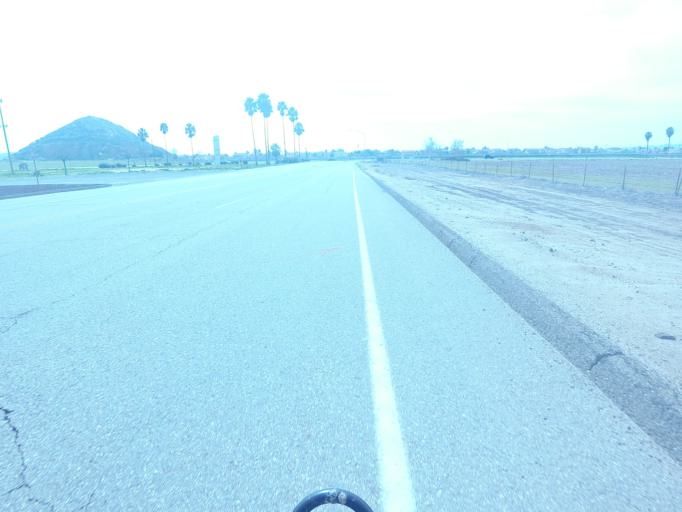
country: US
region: California
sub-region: Riverside County
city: Perris
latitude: 33.8464
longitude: -117.2042
